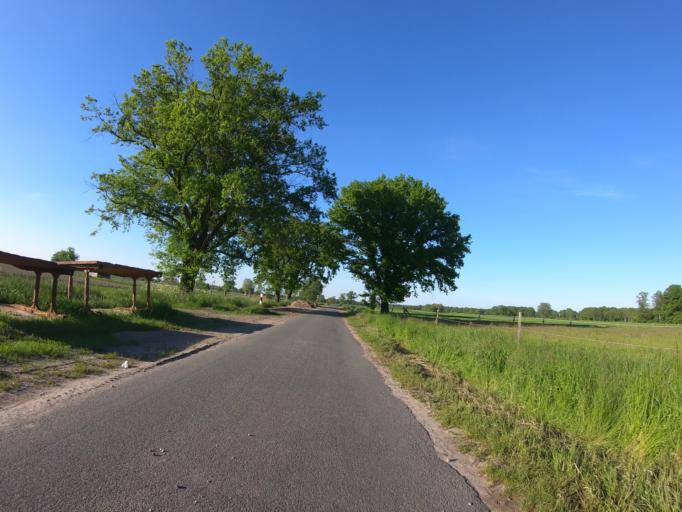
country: DE
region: Lower Saxony
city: Wagenhoff
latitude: 52.5256
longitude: 10.5579
